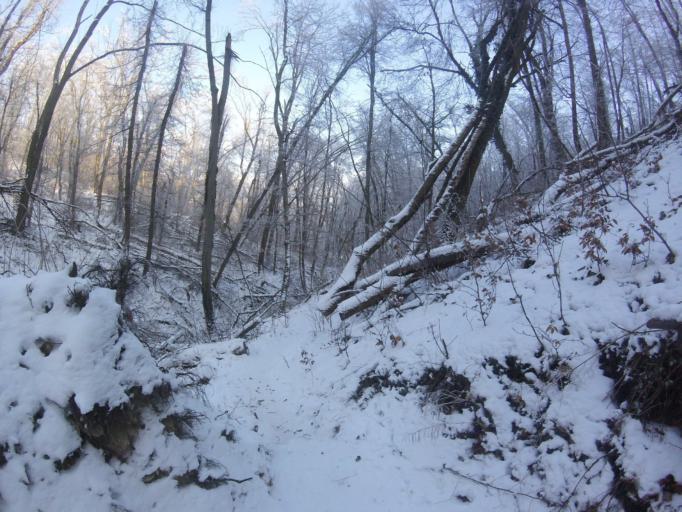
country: HU
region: Pest
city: Pilisszentivan
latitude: 47.5962
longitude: 18.8729
